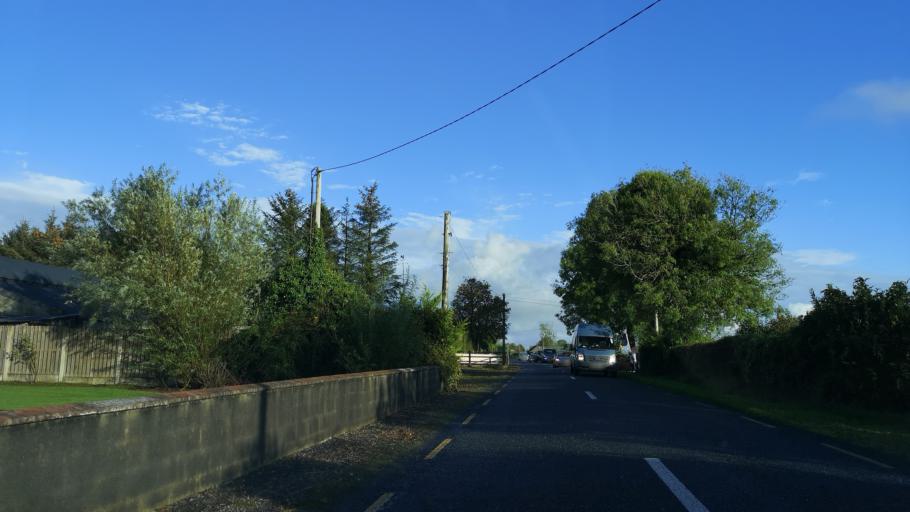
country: IE
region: Connaught
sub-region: Roscommon
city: Castlerea
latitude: 53.8091
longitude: -8.5186
